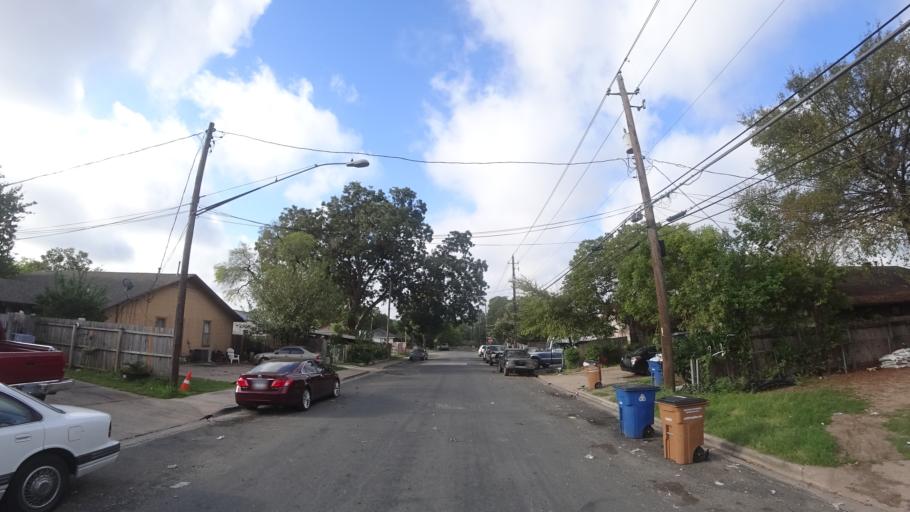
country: US
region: Texas
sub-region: Travis County
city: Austin
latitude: 30.3358
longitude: -97.6961
